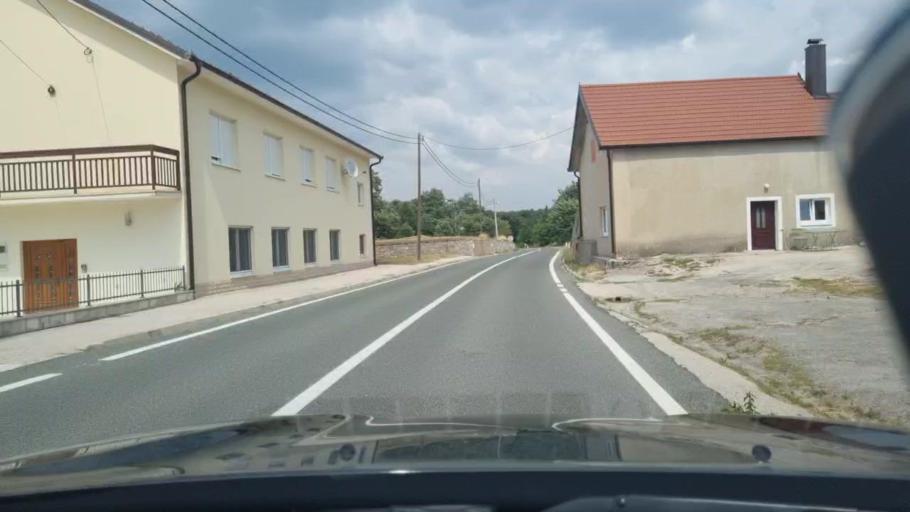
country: BA
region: Federation of Bosnia and Herzegovina
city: Podhum
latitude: 43.6106
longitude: 16.9985
